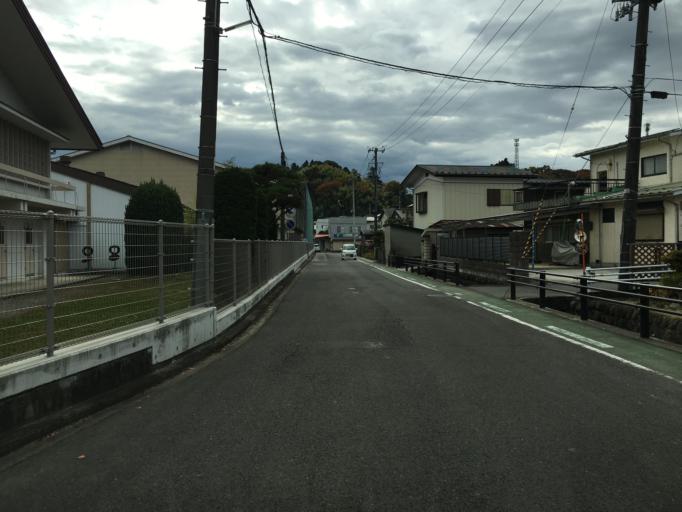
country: JP
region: Fukushima
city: Nihommatsu
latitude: 37.6004
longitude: 140.4398
